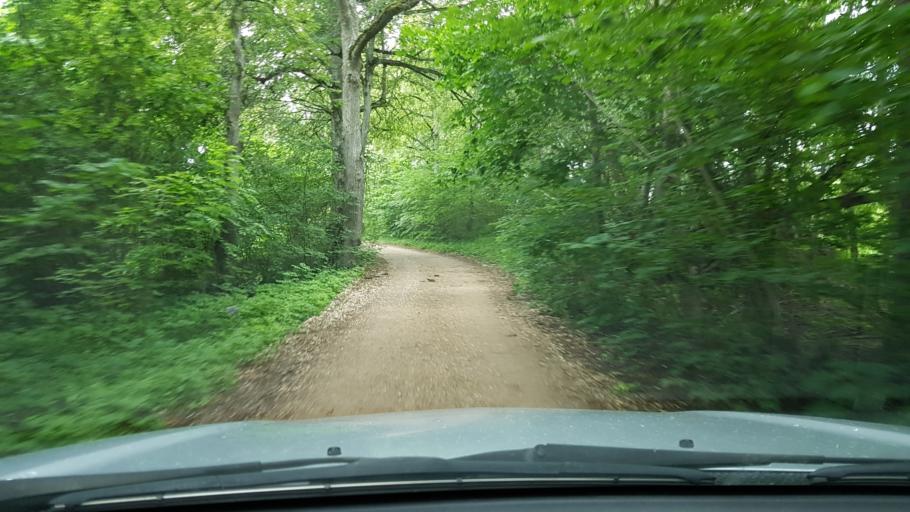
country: EE
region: Ida-Virumaa
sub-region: Narva-Joesuu linn
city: Narva-Joesuu
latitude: 59.3979
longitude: 27.9708
